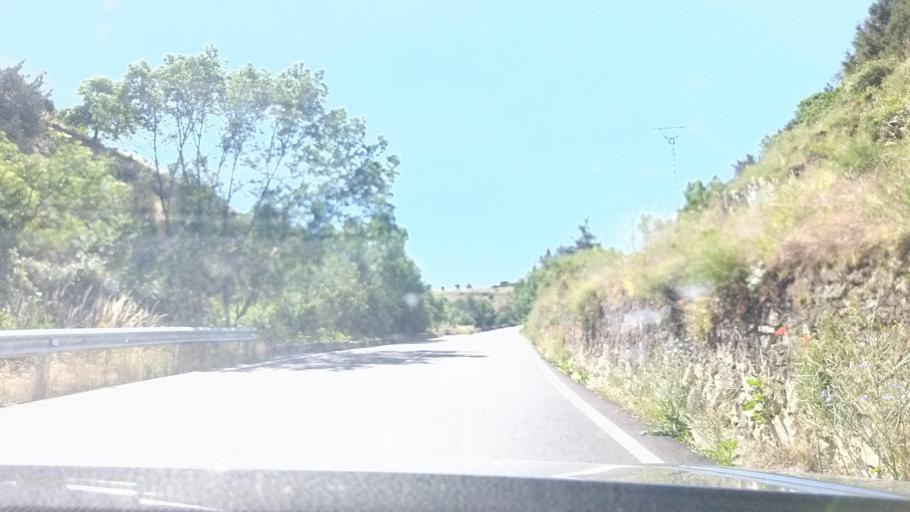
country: ES
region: Castille and Leon
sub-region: Provincia de Segovia
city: Pedraza
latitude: 41.1329
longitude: -3.8106
